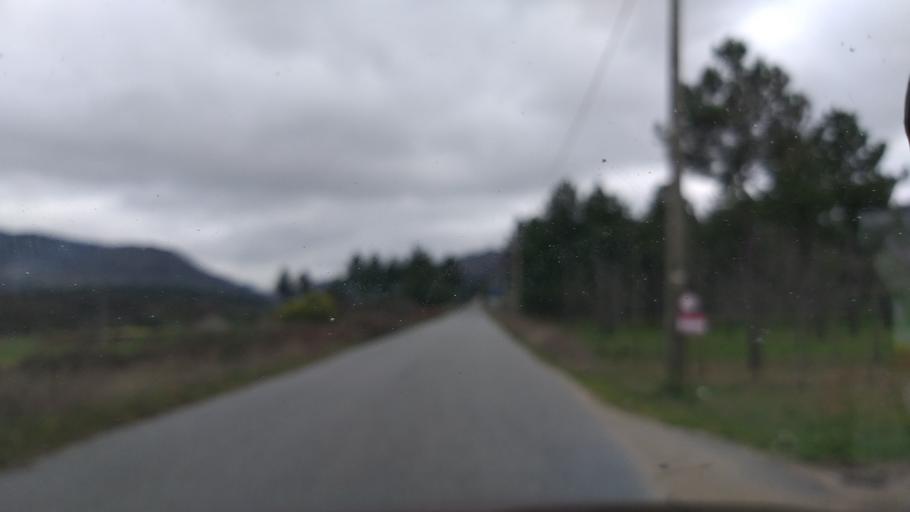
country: PT
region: Guarda
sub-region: Celorico da Beira
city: Celorico da Beira
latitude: 40.7031
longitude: -7.4435
